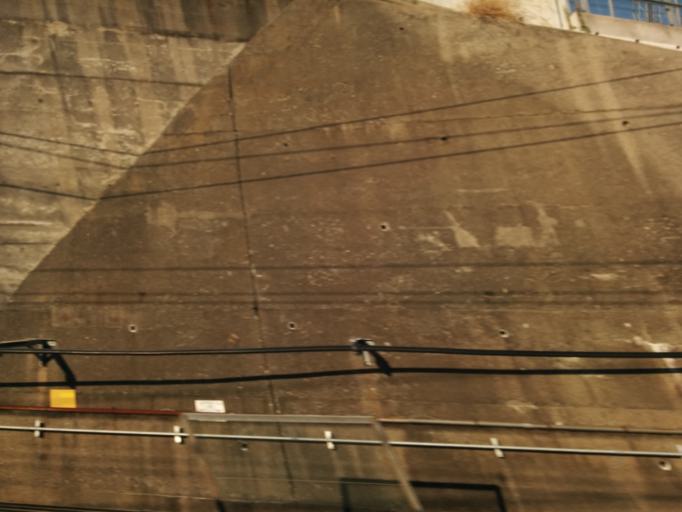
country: JP
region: Aichi
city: Gamagori
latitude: 34.8150
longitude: 137.2810
